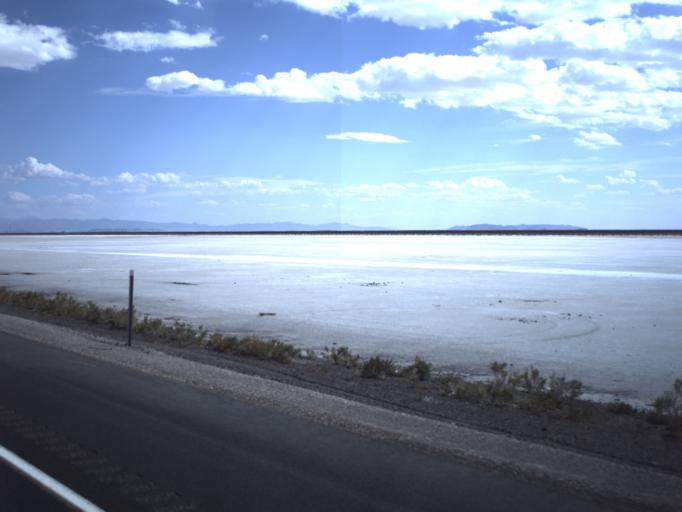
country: US
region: Utah
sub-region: Tooele County
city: Wendover
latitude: 40.7331
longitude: -113.5961
